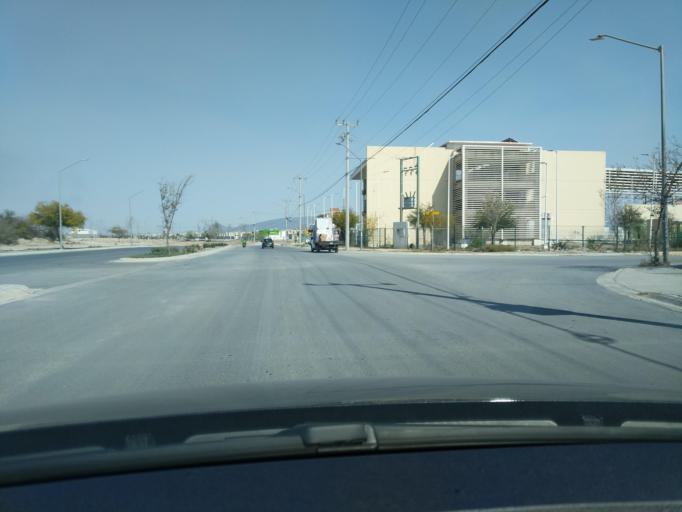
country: MX
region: Nuevo Leon
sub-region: Garcia
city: Los Parques
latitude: 25.7817
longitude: -100.4930
